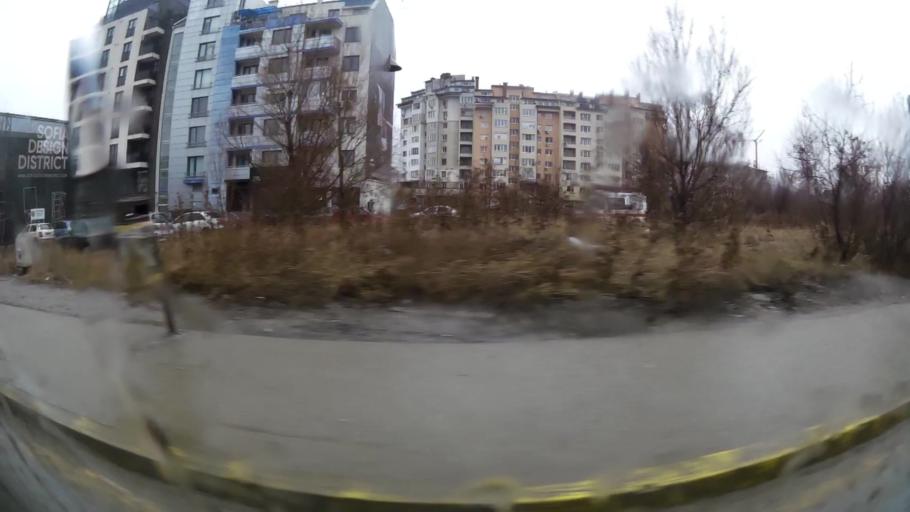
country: BG
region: Sofia-Capital
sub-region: Stolichna Obshtina
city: Sofia
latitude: 42.6384
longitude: 23.3344
